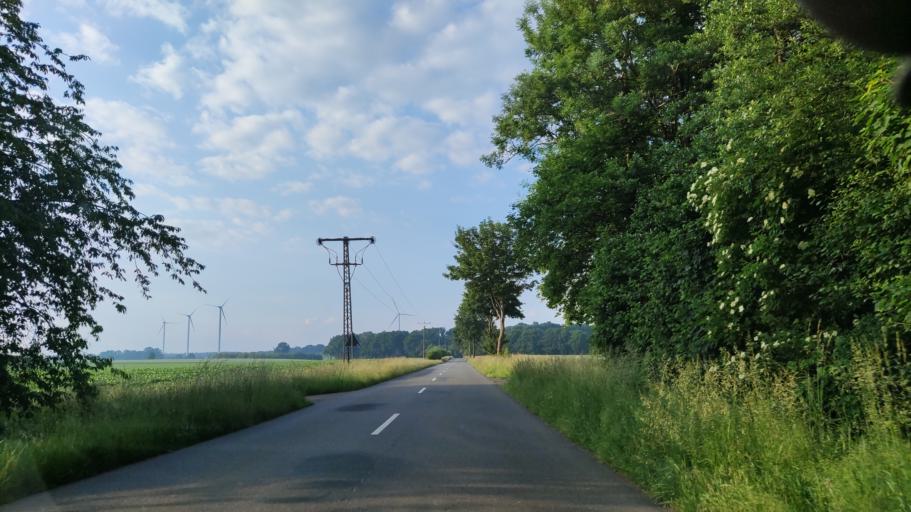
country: DE
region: Lower Saxony
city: Hanstedt Eins
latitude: 53.0353
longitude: 10.3469
